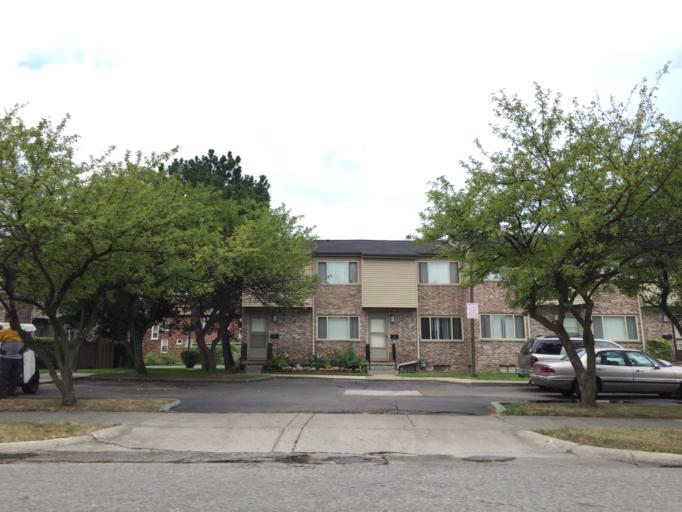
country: US
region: Michigan
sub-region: Wayne County
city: Highland Park
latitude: 42.3687
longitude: -83.0942
